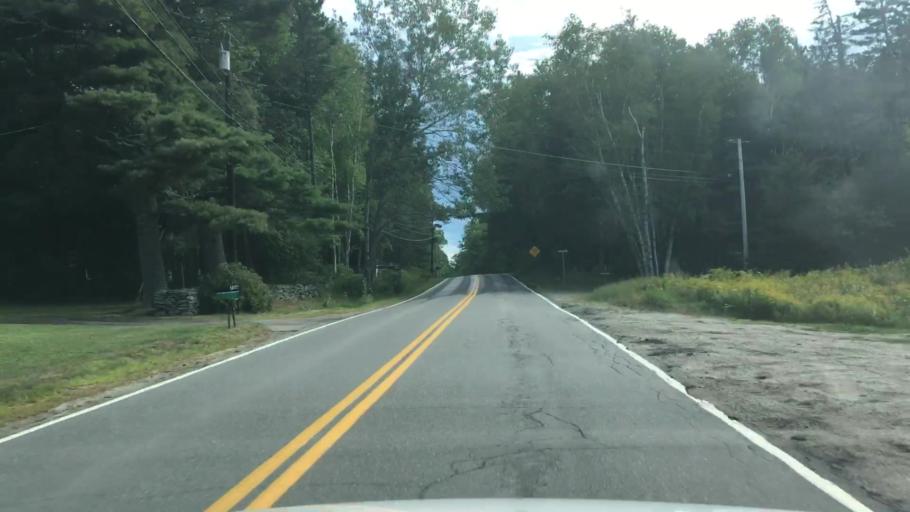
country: US
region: Maine
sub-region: Hancock County
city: Ellsworth
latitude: 44.4812
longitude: -68.4206
